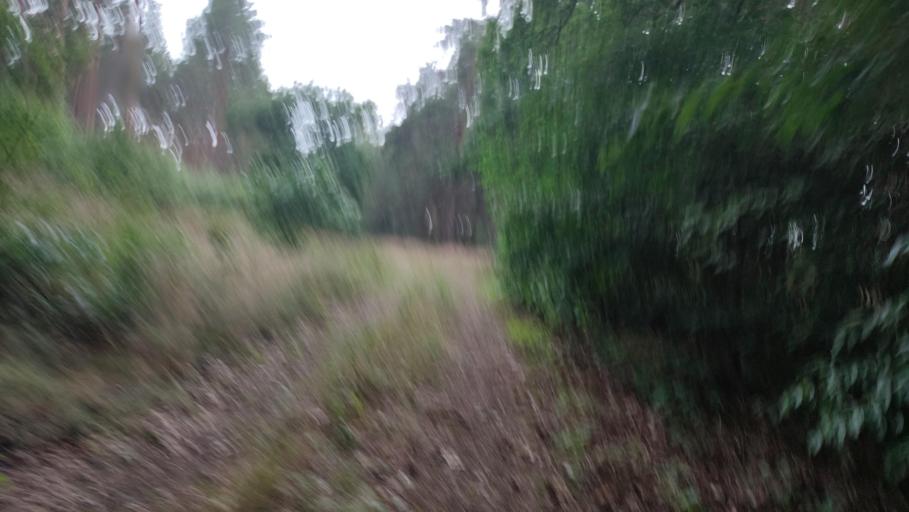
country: DE
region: Lower Saxony
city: Hitzacker
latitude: 53.2022
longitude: 11.0871
